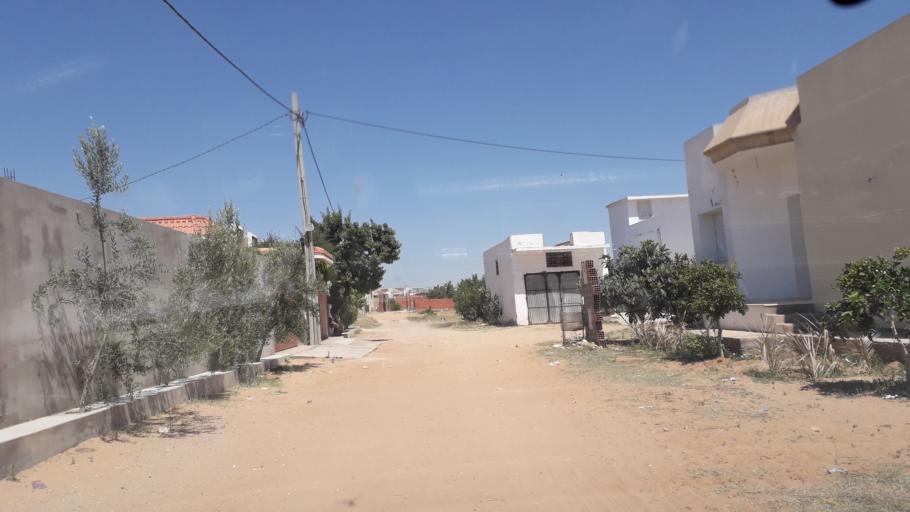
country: TN
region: Safaqis
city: Al Qarmadah
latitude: 34.8248
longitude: 10.7675
